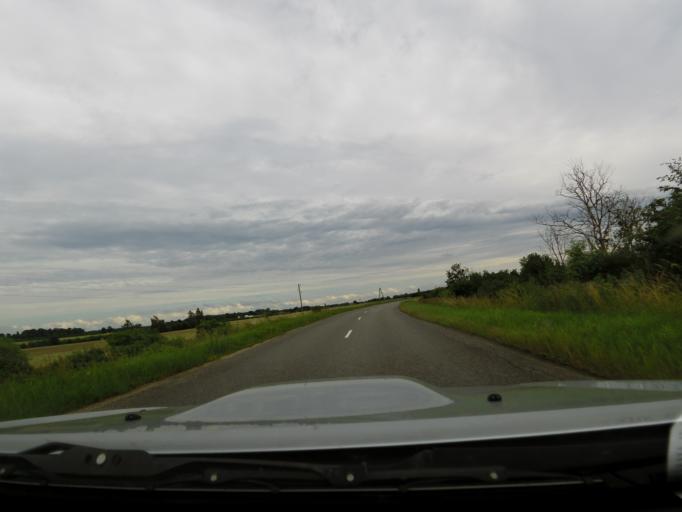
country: LV
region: Rundales
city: Pilsrundale
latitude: 56.5822
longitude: 23.9707
